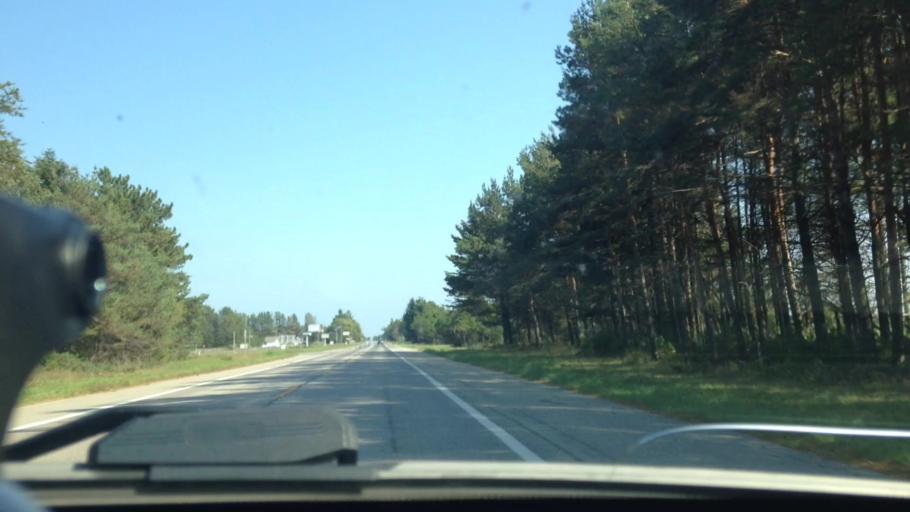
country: US
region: Michigan
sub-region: Luce County
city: Newberry
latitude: 46.3034
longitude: -85.4747
